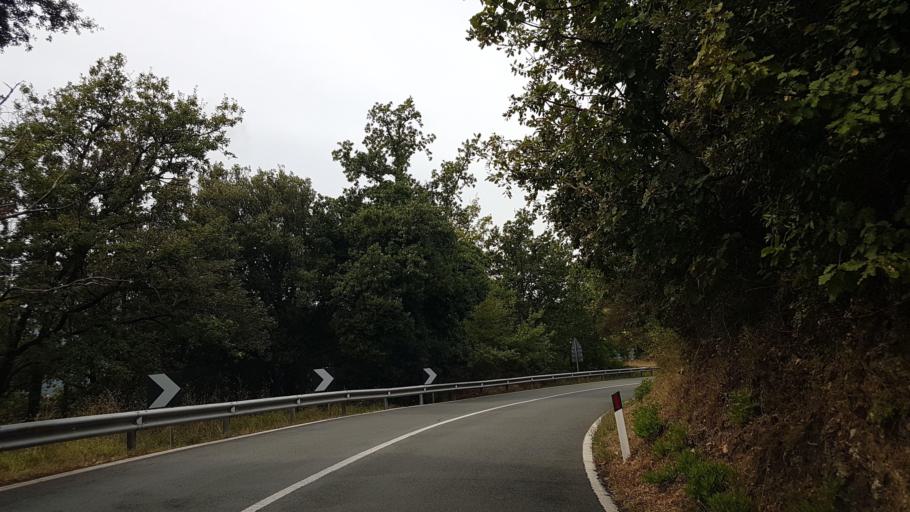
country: IT
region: Liguria
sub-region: Provincia di Genova
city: Moneglia
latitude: 44.2574
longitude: 9.4943
